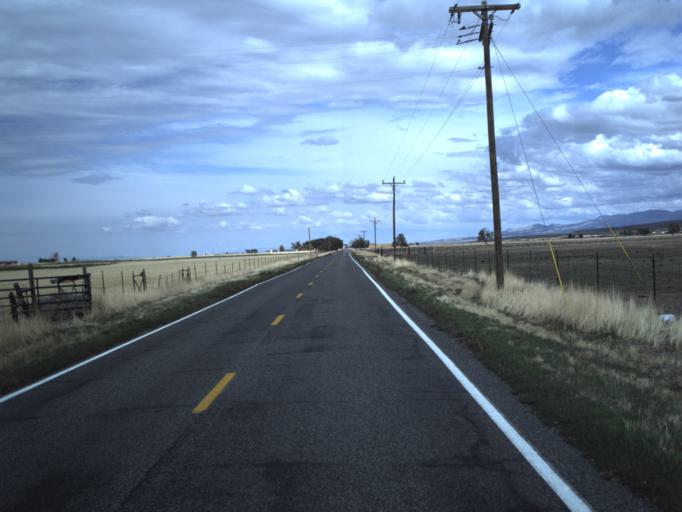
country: US
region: Utah
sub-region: Millard County
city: Fillmore
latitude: 39.0319
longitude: -112.4099
